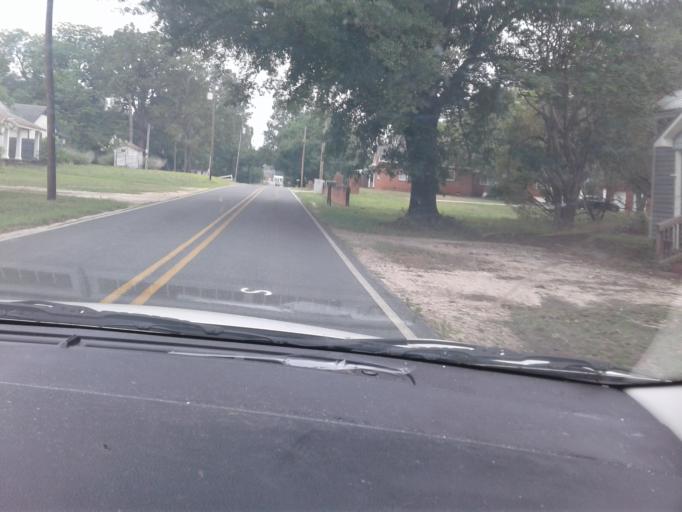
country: US
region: North Carolina
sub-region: Harnett County
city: Buies Creek
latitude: 35.4122
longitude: -78.7310
